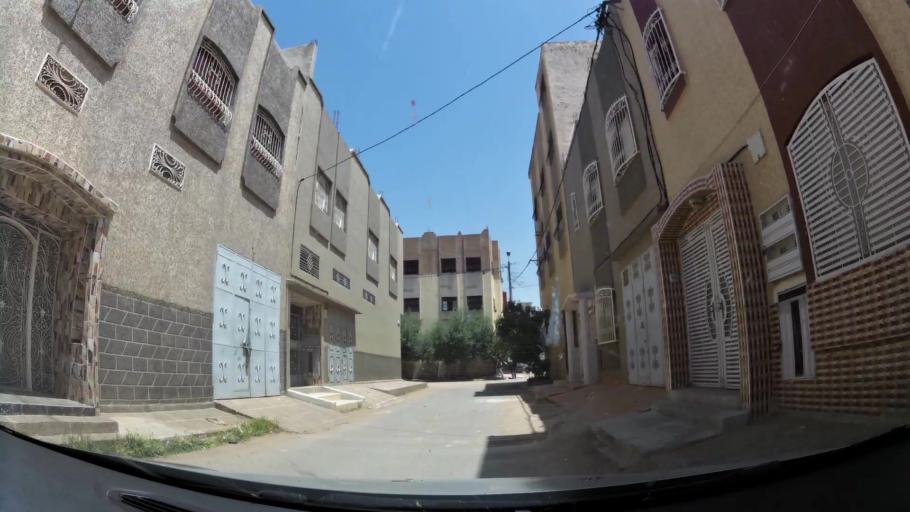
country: MA
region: Rabat-Sale-Zemmour-Zaer
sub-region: Khemisset
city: Khemisset
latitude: 33.8245
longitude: -6.0789
